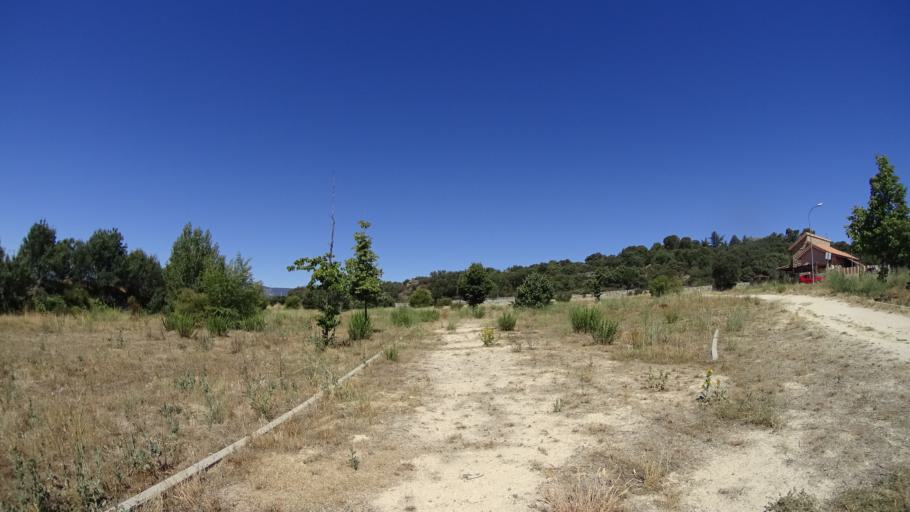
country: ES
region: Madrid
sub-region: Provincia de Madrid
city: Alpedrete
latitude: 40.6490
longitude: -4.0291
